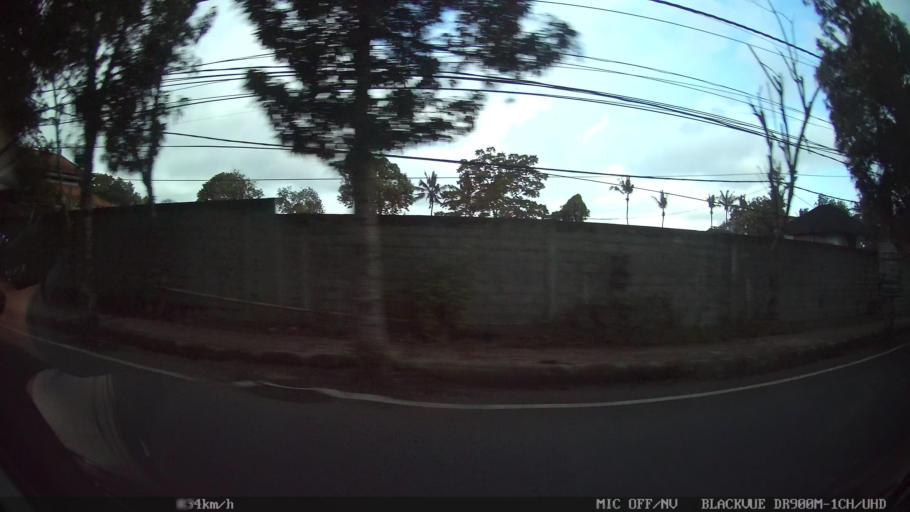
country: ID
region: Bali
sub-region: Kabupaten Gianyar
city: Ubud
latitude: -8.4941
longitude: 115.2535
